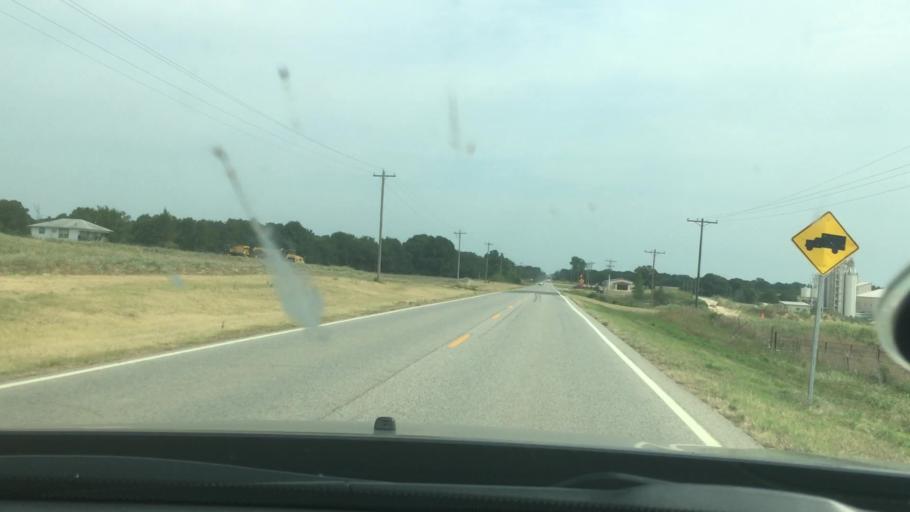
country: US
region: Oklahoma
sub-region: Bryan County
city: Durant
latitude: 34.2107
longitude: -96.4250
